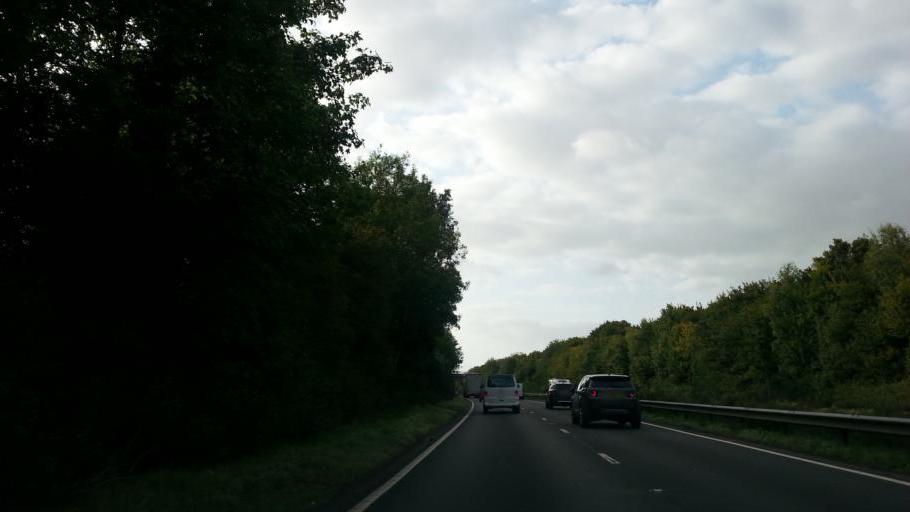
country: GB
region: England
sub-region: Hampshire
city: Kings Worthy
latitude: 51.0928
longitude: -1.3082
